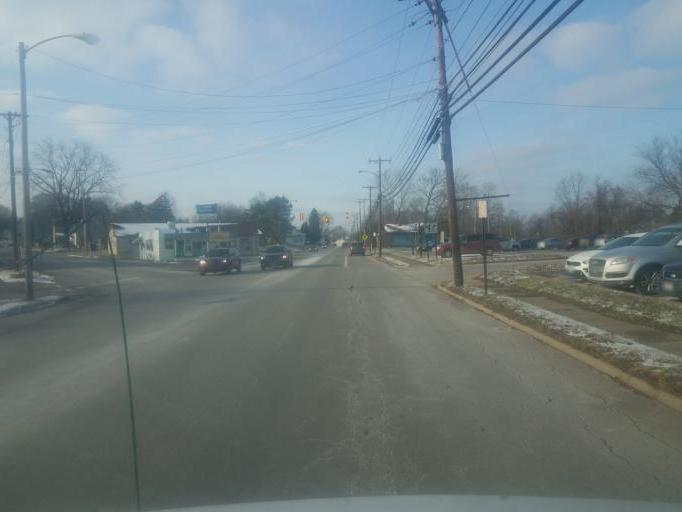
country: US
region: Ohio
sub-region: Richland County
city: Mansfield
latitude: 40.7484
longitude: -82.5092
